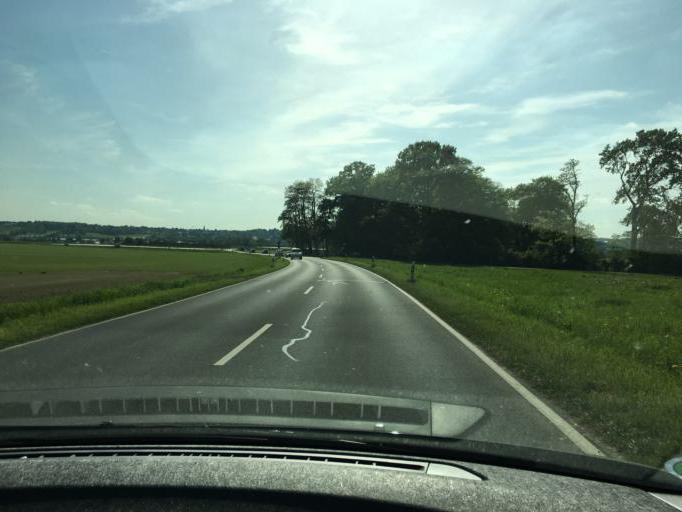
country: DE
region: North Rhine-Westphalia
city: Bornheim
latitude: 50.7834
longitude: 6.9501
